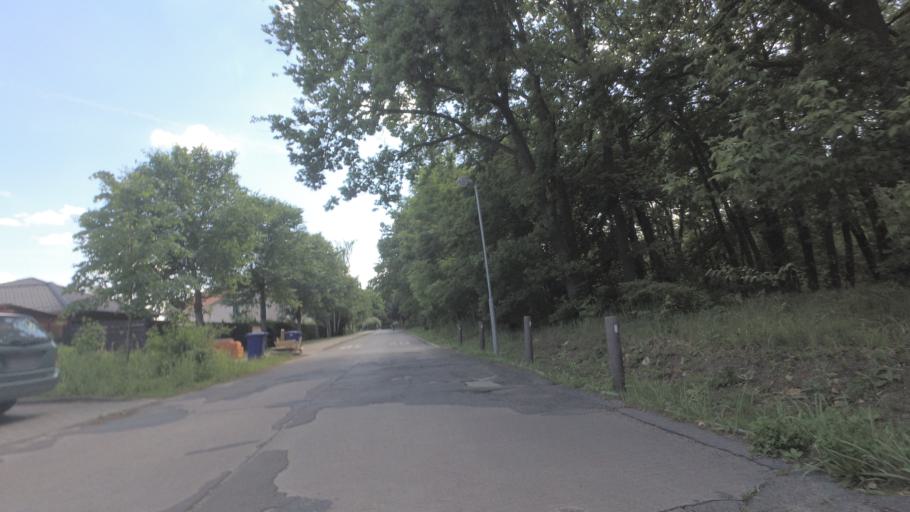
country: DE
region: Brandenburg
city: Rangsdorf
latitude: 52.2834
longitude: 13.4183
